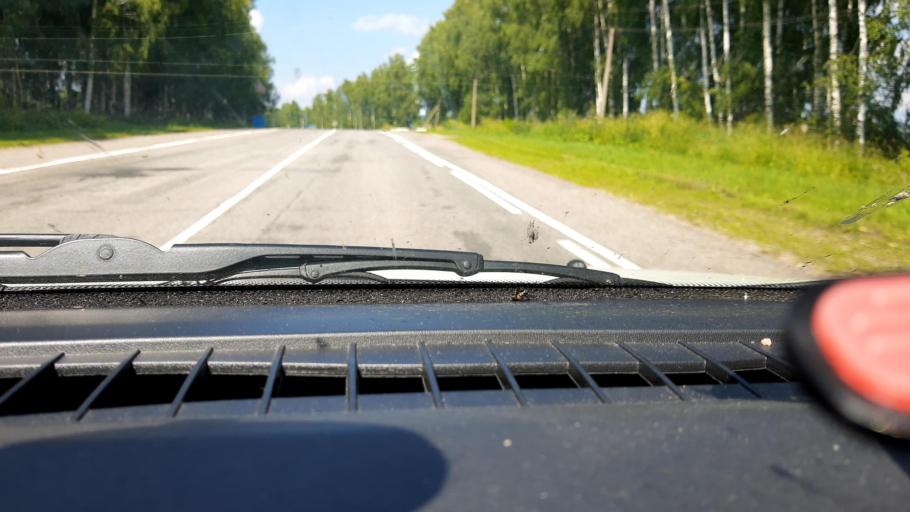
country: RU
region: Nizjnij Novgorod
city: Tonkino
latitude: 57.2693
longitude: 46.4603
